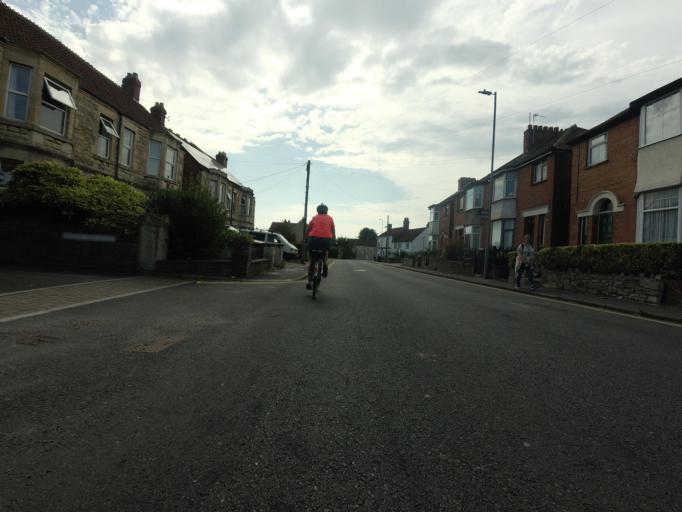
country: GB
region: England
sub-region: Wiltshire
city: Trowbridge
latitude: 51.3265
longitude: -2.2041
